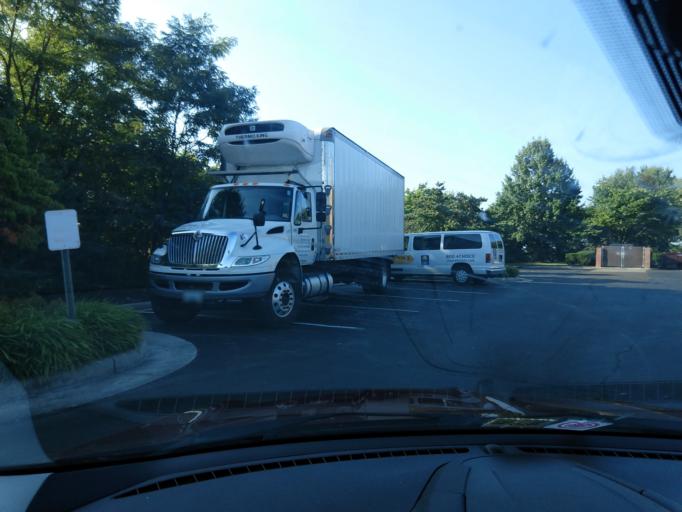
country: US
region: Virginia
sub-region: Montgomery County
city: Merrimac
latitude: 37.1850
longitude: -80.4076
